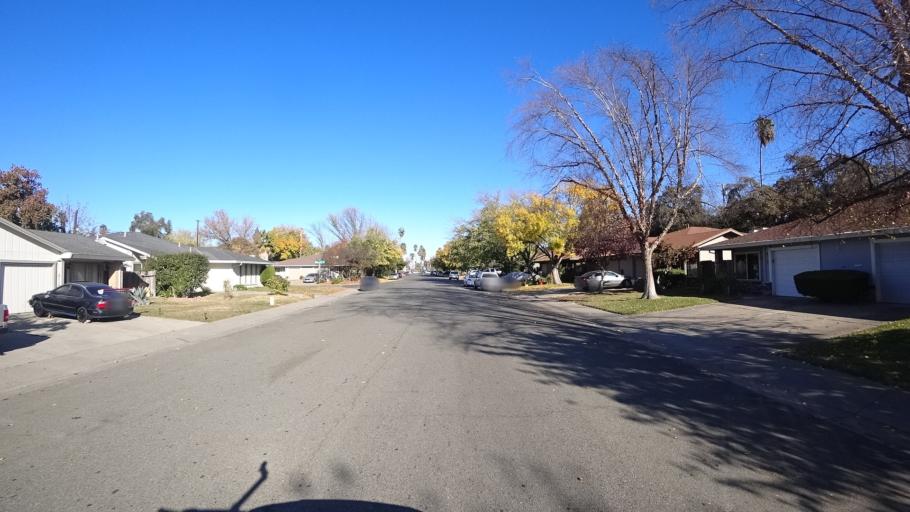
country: US
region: California
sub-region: Sacramento County
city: Citrus Heights
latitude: 38.6761
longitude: -121.2984
